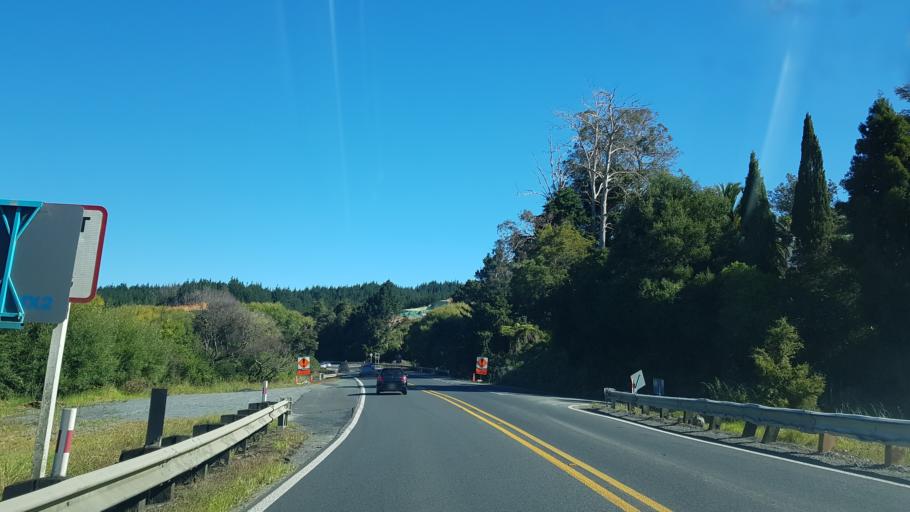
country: NZ
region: Auckland
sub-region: Auckland
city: Warkworth
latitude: -36.4911
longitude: 174.6591
